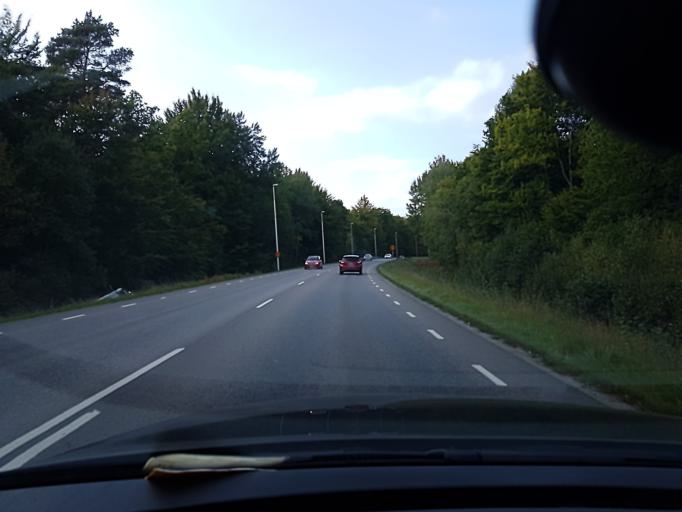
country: SE
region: Kronoberg
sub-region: Vaxjo Kommun
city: Vaexjoe
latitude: 56.8643
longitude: 14.7945
